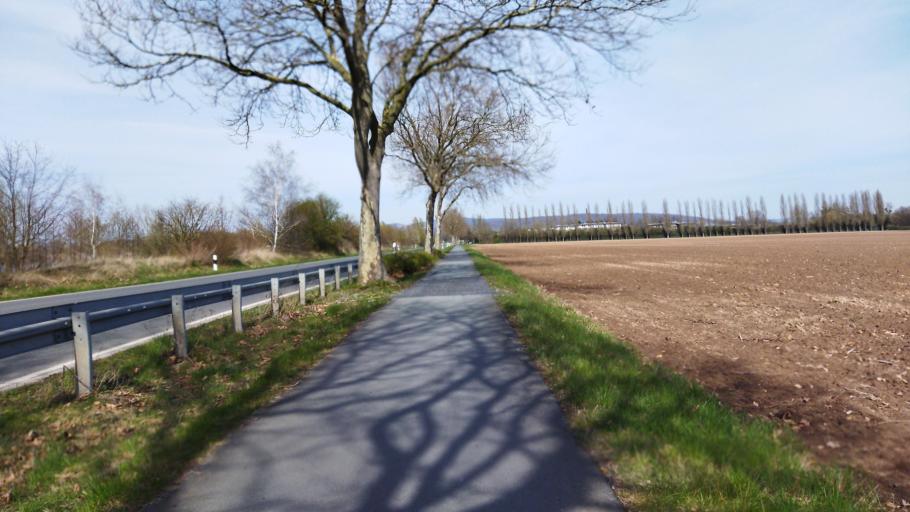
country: DE
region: Lower Saxony
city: Hameln
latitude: 52.0727
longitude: 9.3778
